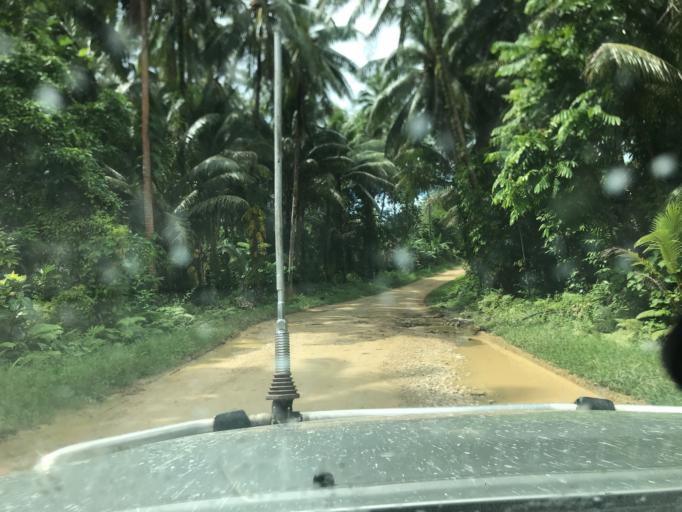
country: SB
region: Malaita
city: Auki
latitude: -8.3509
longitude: 160.6421
